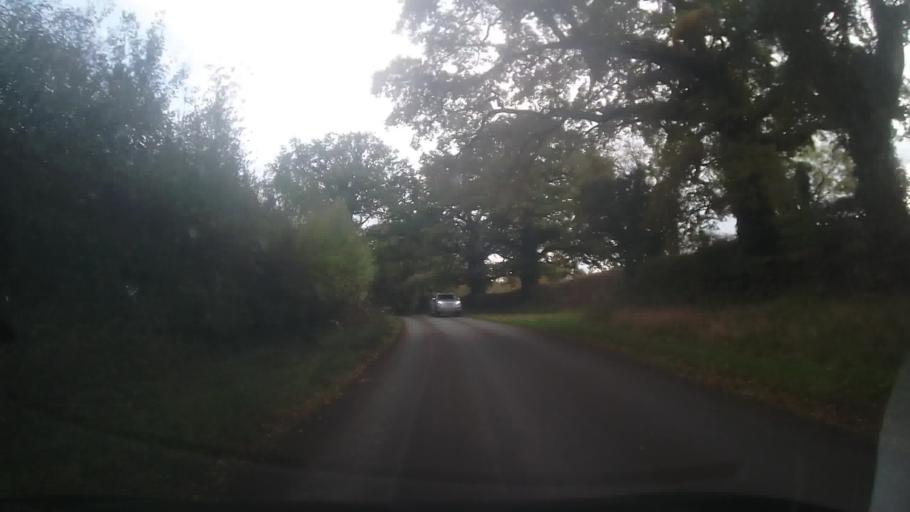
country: GB
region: England
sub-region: Shropshire
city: Wem
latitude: 52.8894
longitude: -2.7529
